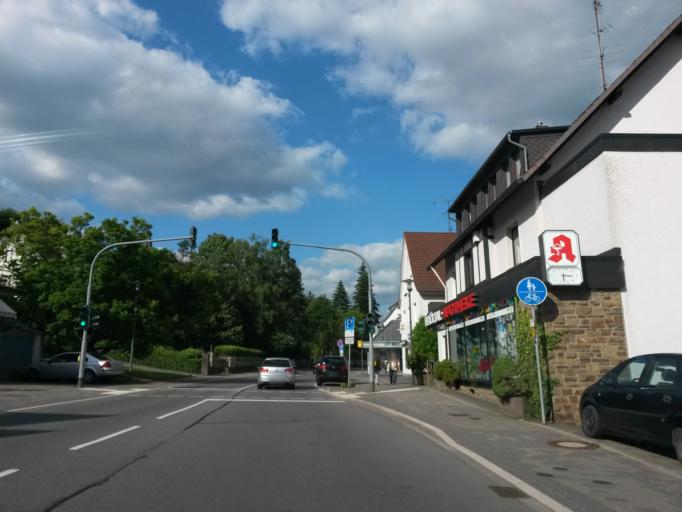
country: DE
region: North Rhine-Westphalia
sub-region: Regierungsbezirk Koln
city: Ruppichteroth
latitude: 50.8429
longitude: 7.4808
